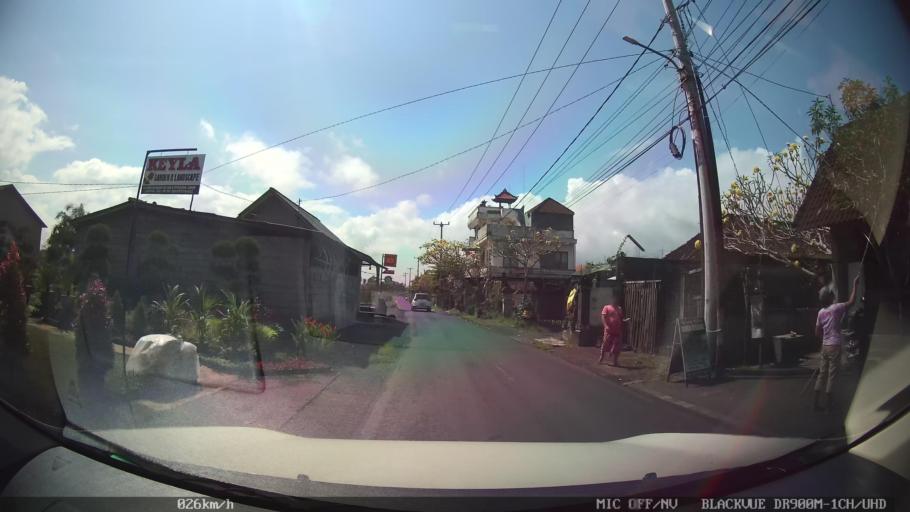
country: ID
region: Bali
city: Banjar Sedang
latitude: -8.5606
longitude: 115.2640
